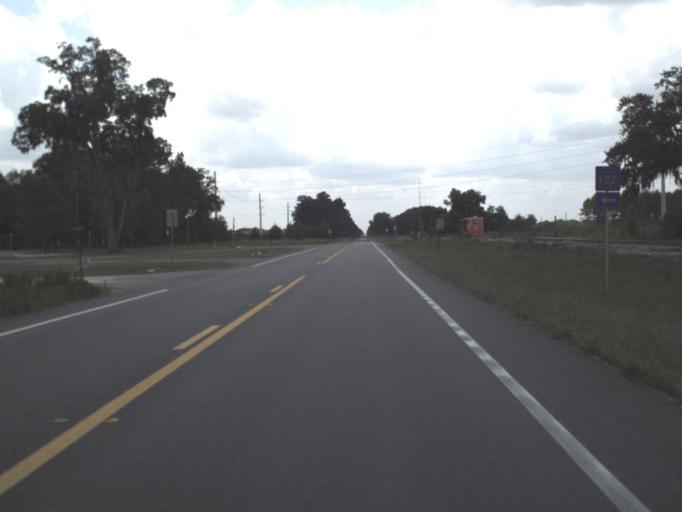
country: US
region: Florida
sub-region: Hamilton County
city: Jasper
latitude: 30.3993
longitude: -82.8342
